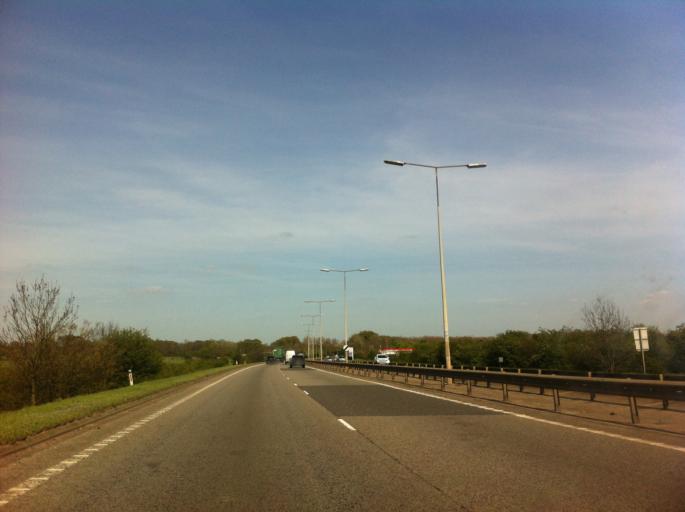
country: GB
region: England
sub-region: Northamptonshire
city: Earls Barton
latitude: 52.2542
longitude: -0.7983
